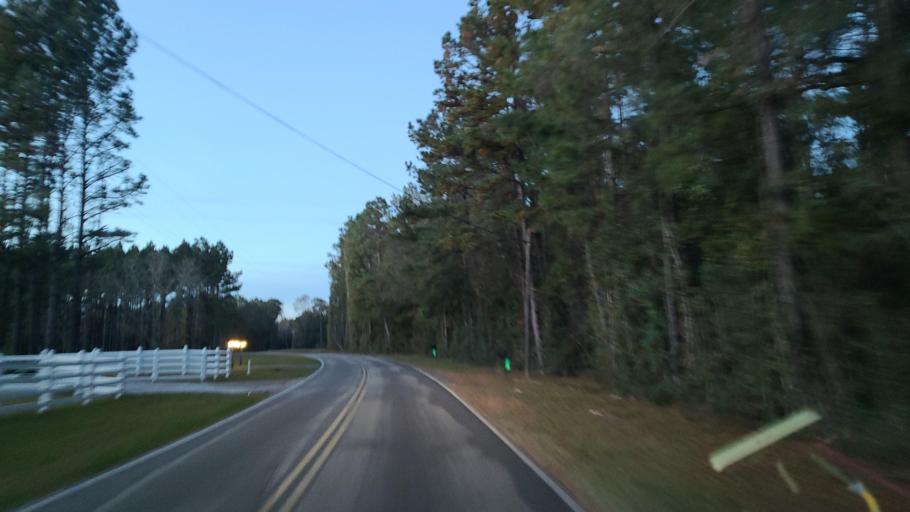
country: US
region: Mississippi
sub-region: Forrest County
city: Hattiesburg
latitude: 31.1761
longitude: -89.2190
